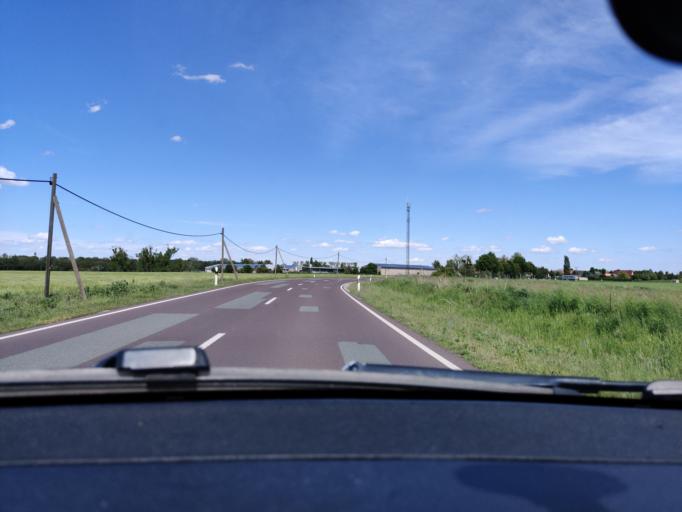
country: DE
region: Saxony-Anhalt
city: Mockern
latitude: 52.1277
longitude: 11.9495
